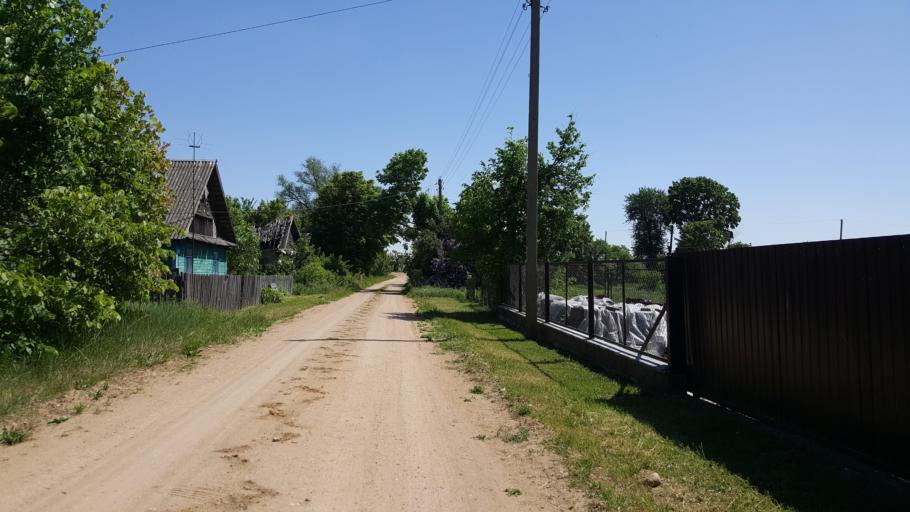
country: BY
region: Brest
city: Charnawchytsy
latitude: 52.2768
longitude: 23.7930
